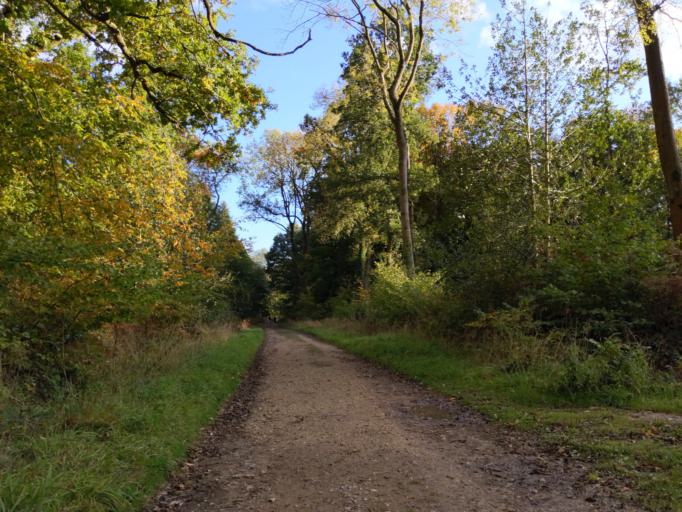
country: GB
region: England
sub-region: Oxfordshire
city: Radley
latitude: 51.7171
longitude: -1.2577
